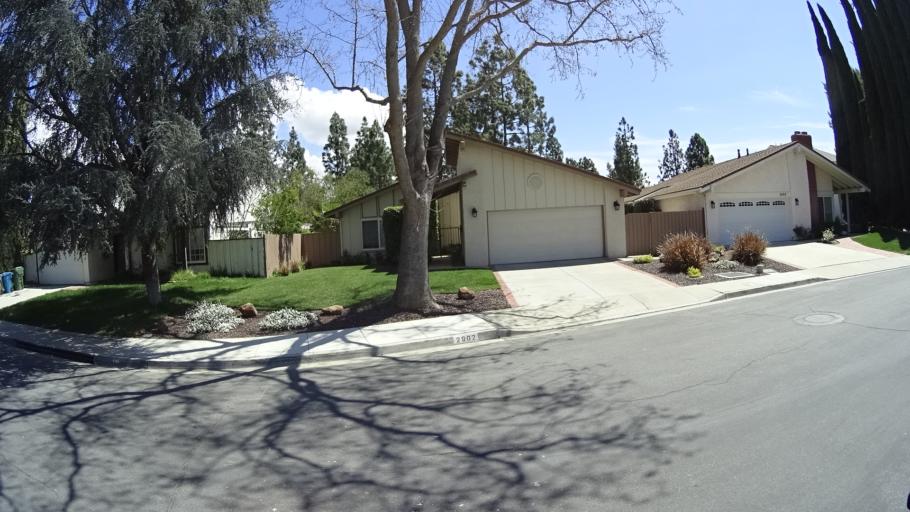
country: US
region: California
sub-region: Ventura County
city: Thousand Oaks
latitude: 34.2177
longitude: -118.8431
